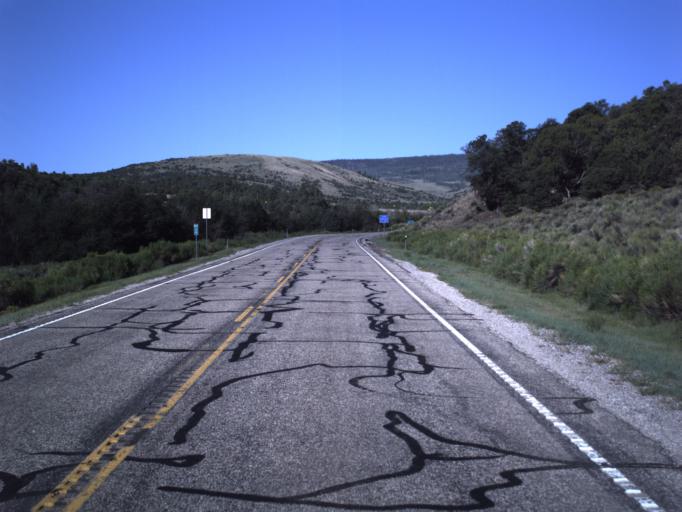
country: US
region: Utah
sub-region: Wayne County
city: Loa
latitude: 38.6504
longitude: -111.4382
